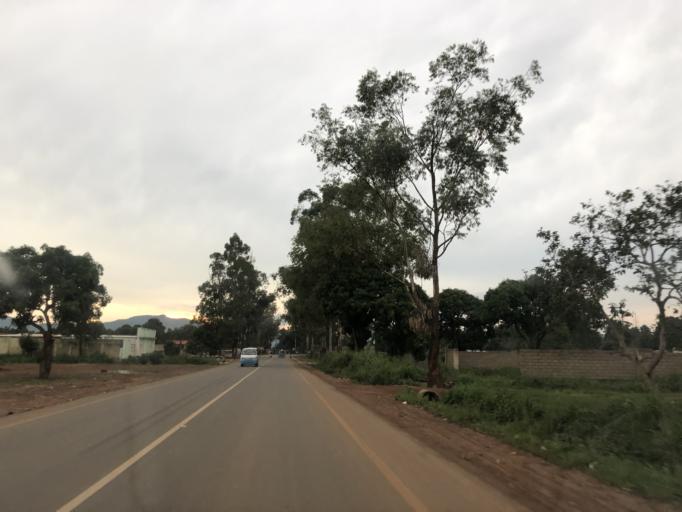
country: AO
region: Cuanza Sul
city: Uacu Cungo
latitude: -11.3519
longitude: 15.1156
